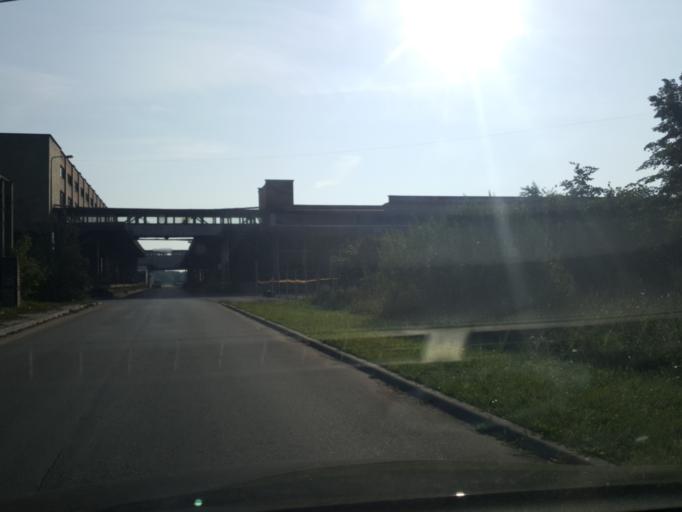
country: LT
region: Alytaus apskritis
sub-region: Alytus
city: Alytus
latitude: 54.4351
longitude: 24.0190
